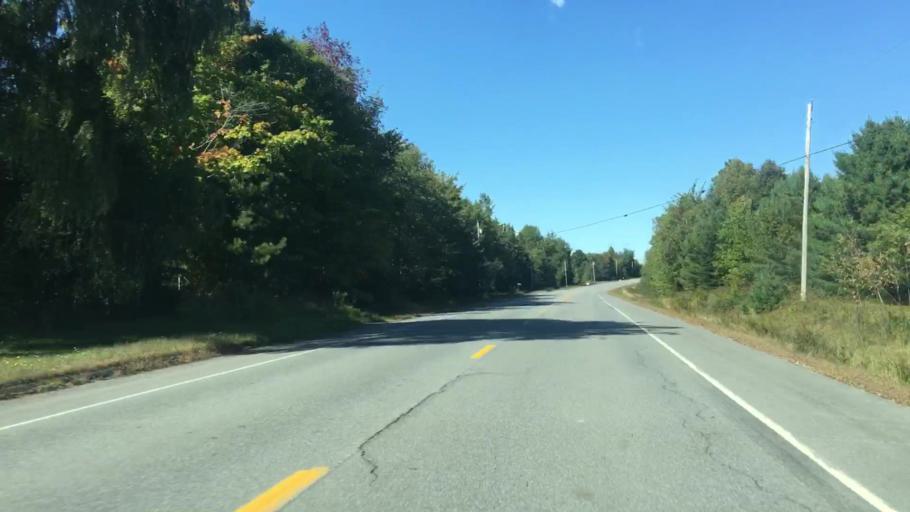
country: US
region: Maine
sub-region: Piscataquis County
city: Sangerville
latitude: 45.0676
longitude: -69.4587
